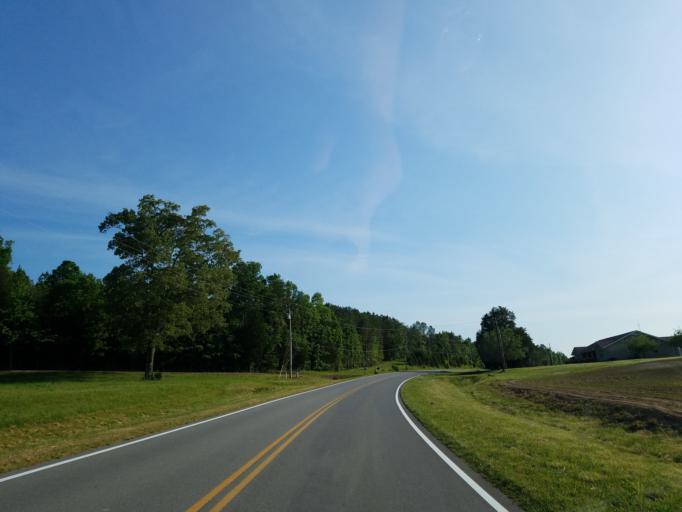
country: US
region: Georgia
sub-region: Chattooga County
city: Trion
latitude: 34.5129
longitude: -85.2313
